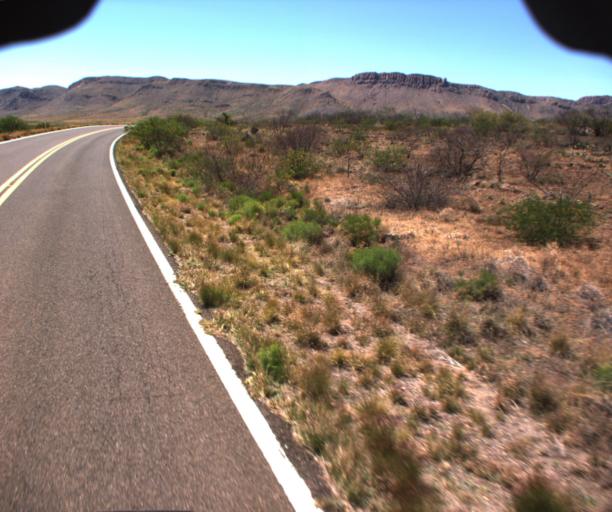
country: US
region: Arizona
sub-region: Cochise County
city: Douglas
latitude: 31.4646
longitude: -109.3630
